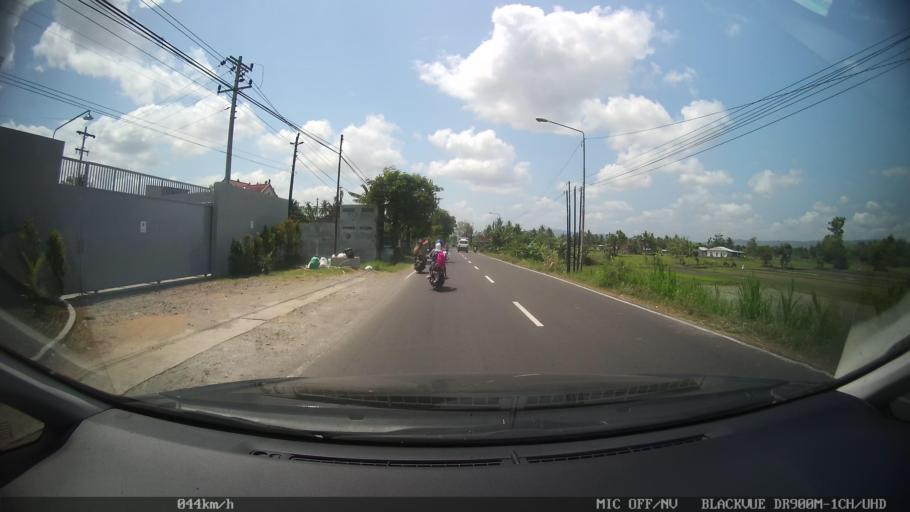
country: ID
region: Daerah Istimewa Yogyakarta
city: Bantul
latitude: -7.9050
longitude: 110.3234
